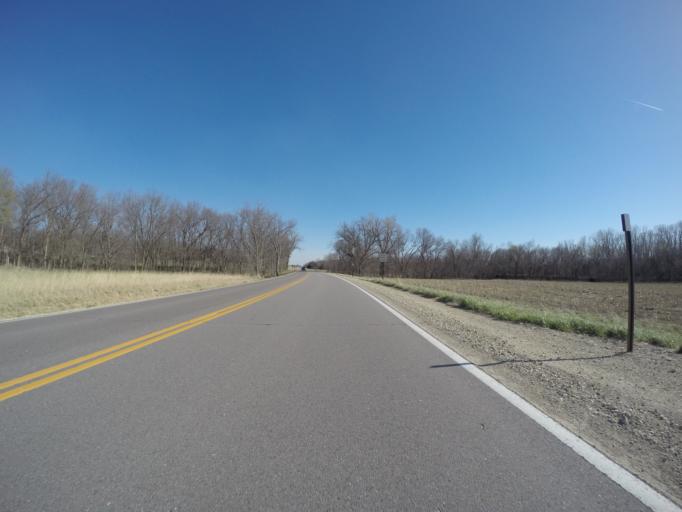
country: US
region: Kansas
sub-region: Riley County
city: Fort Riley North
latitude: 39.2579
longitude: -96.7750
